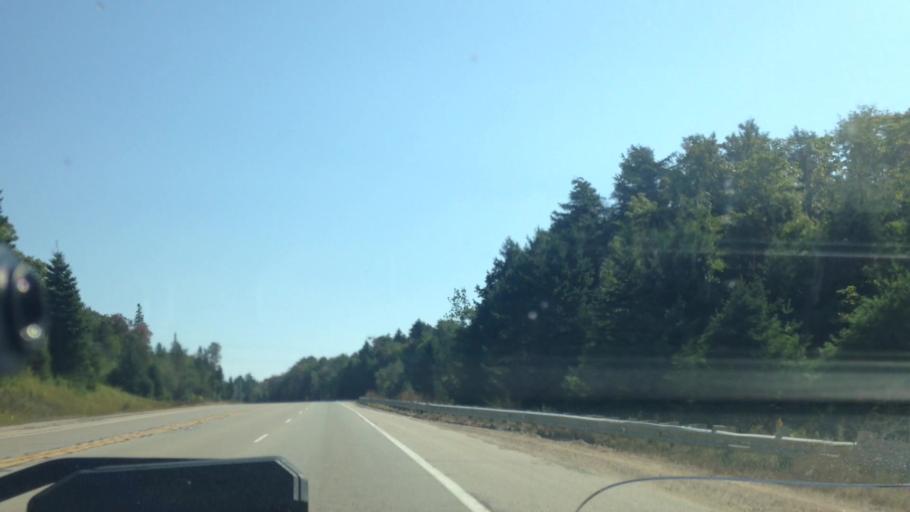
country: US
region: Michigan
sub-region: Alger County
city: Munising
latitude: 46.3879
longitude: -86.6443
